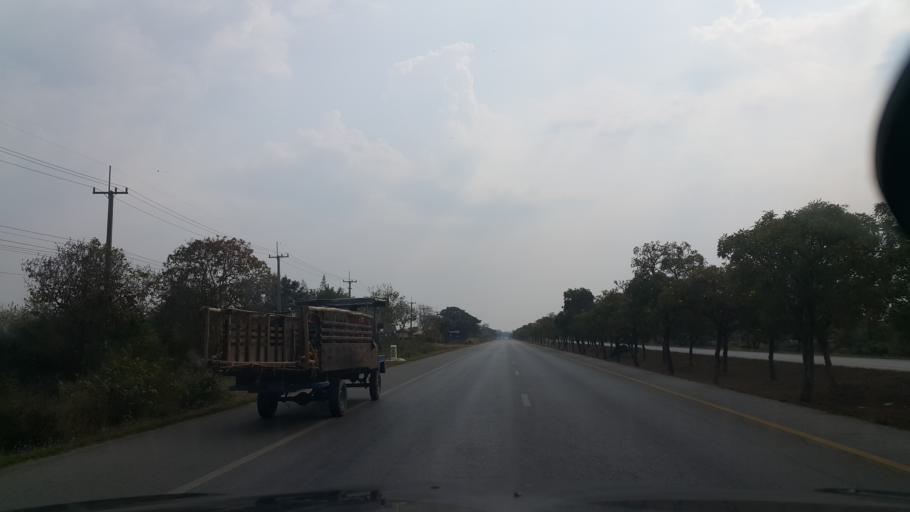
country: TH
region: Sukhothai
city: Sukhothai
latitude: 17.0628
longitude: 99.8821
